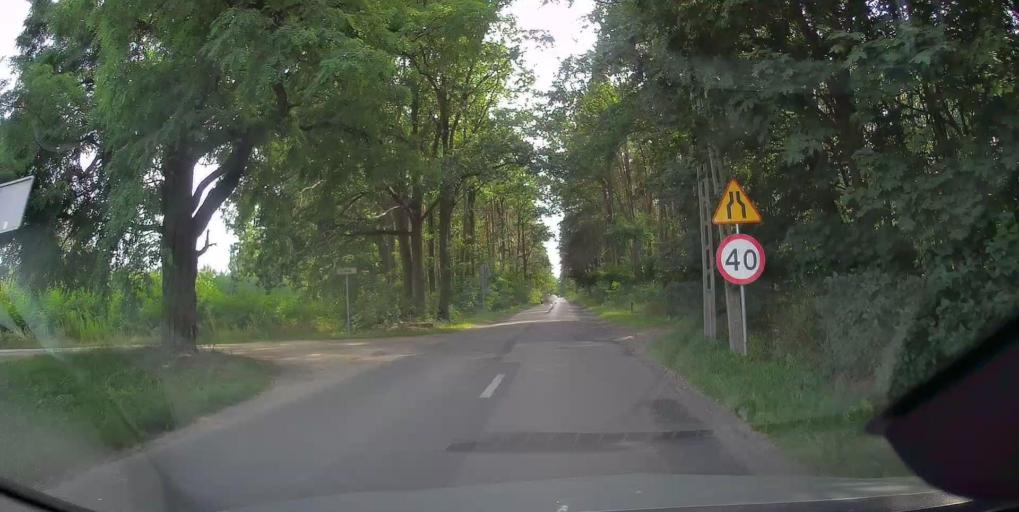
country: PL
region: Lodz Voivodeship
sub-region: Powiat tomaszowski
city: Tomaszow Mazowiecki
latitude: 51.4815
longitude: 19.9878
